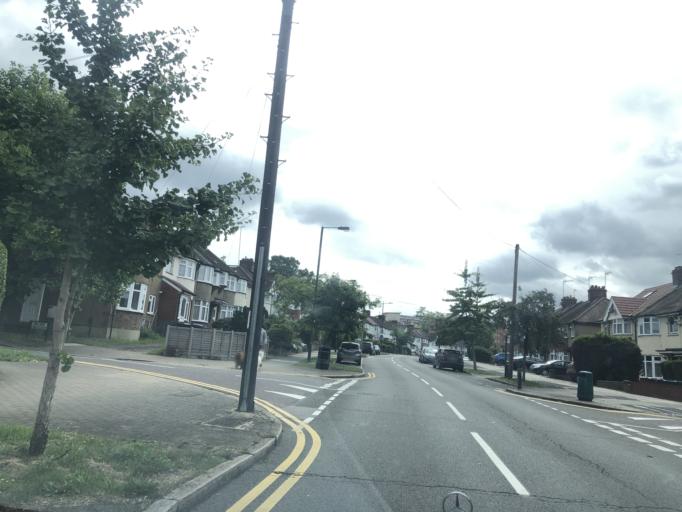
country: GB
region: England
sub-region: Greater London
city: Greenhill
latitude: 51.5704
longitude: -0.3552
